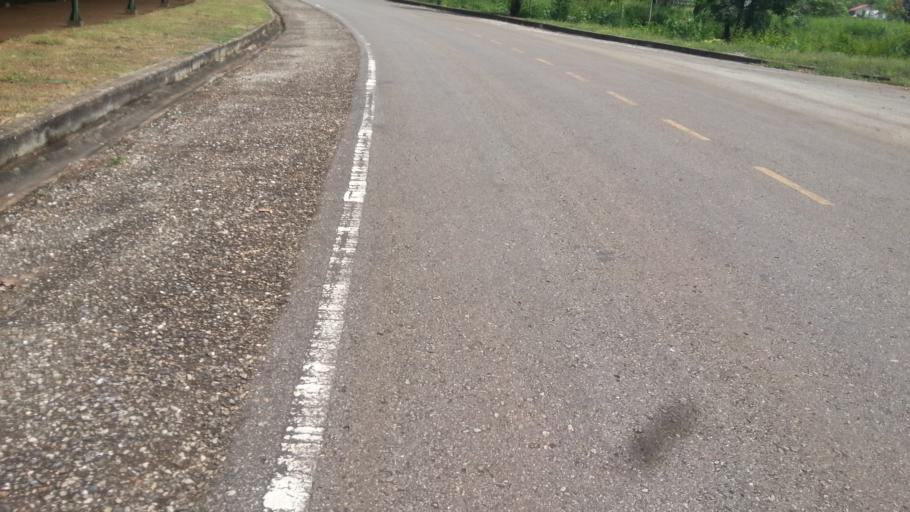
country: TH
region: Kanchanaburi
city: Sai Yok
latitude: 14.1289
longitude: 99.1607
